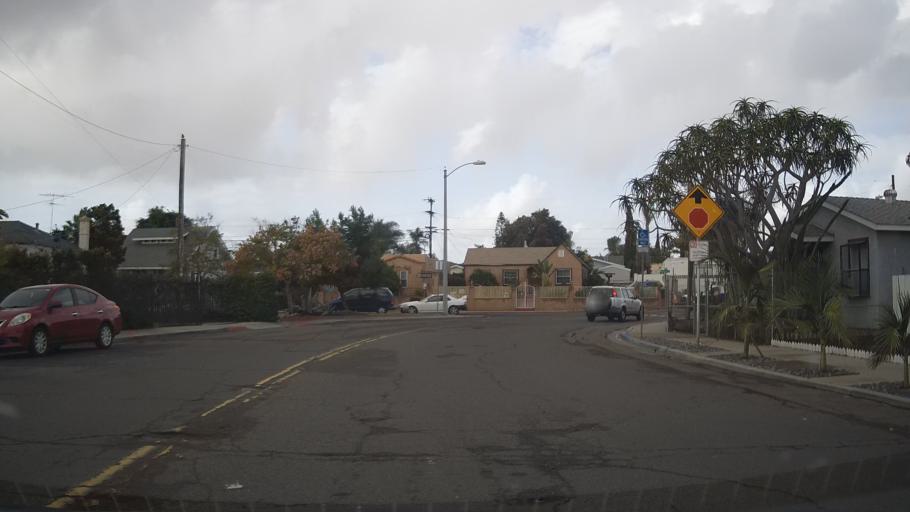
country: US
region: California
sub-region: San Diego County
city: San Diego
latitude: 32.7456
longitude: -117.1216
